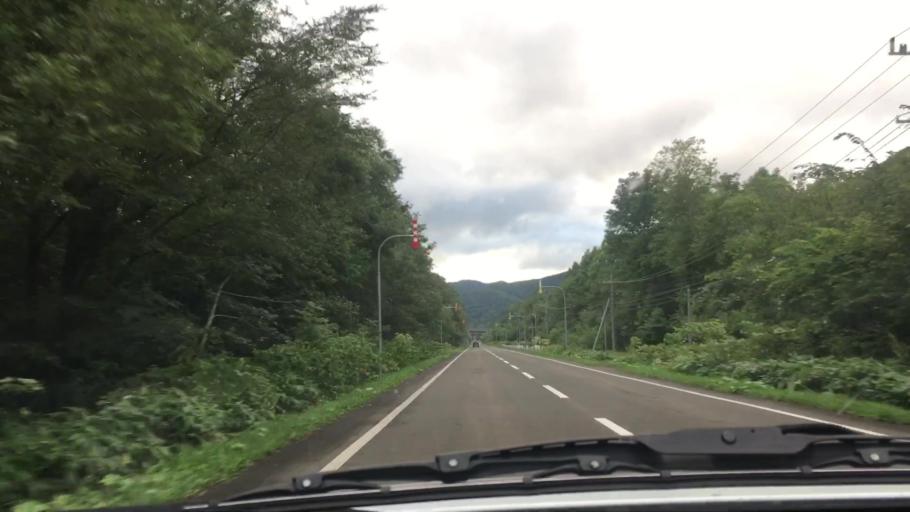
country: JP
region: Hokkaido
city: Shimo-furano
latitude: 43.0558
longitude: 142.5743
